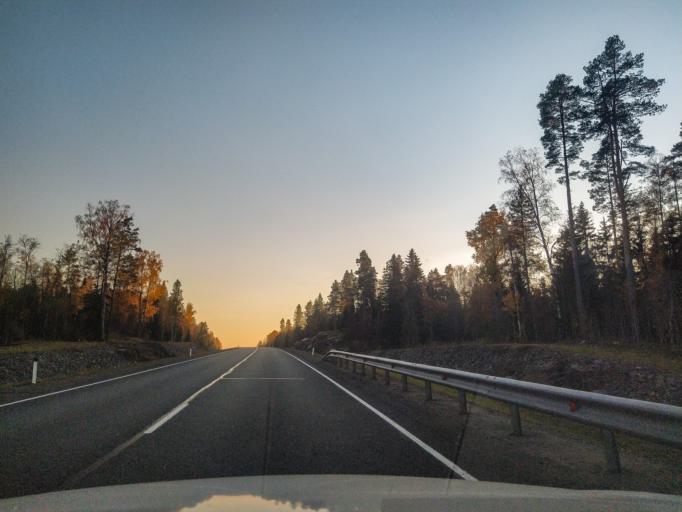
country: RU
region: Leningrad
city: Kuznechnoye
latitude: 61.3620
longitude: 29.8946
